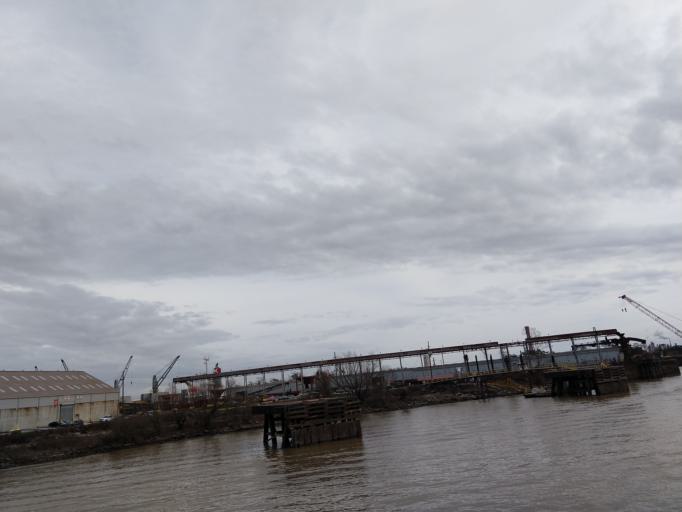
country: US
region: Louisiana
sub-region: Saint Bernard Parish
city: Arabi
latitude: 29.9418
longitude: -89.9999
